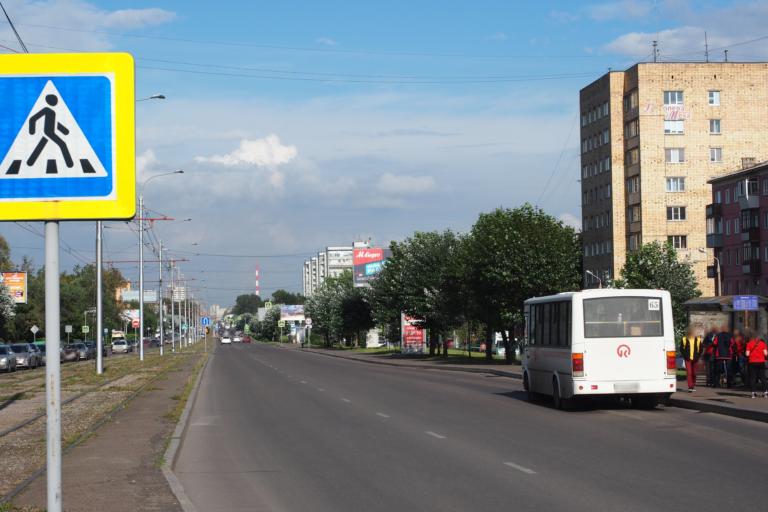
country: RU
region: Krasnoyarskiy
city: Krasnoyarsk
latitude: 55.9944
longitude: 92.8974
